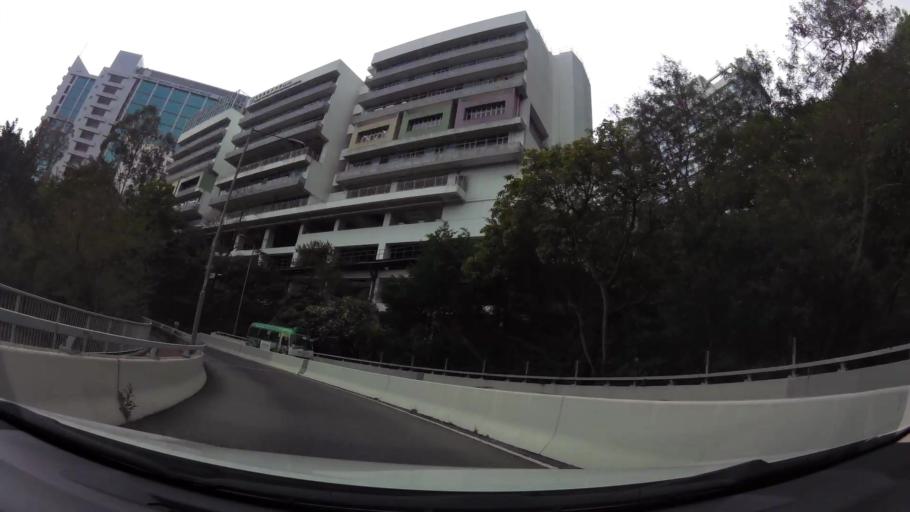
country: HK
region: Central and Western
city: Central
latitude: 22.2677
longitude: 114.1304
